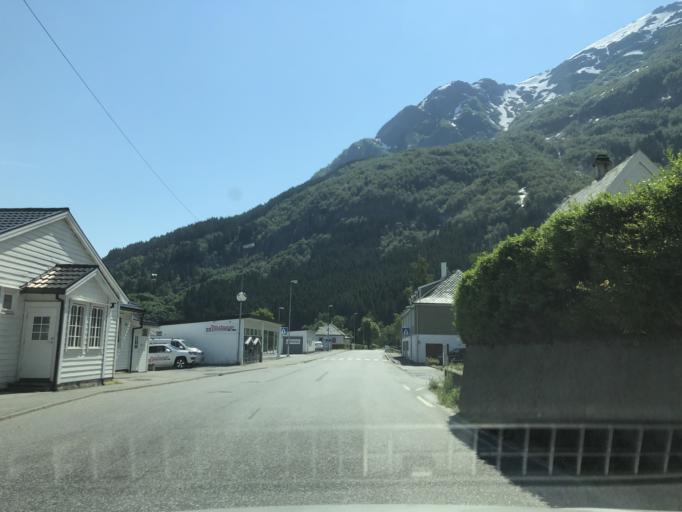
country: NO
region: Hordaland
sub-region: Odda
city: Odda
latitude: 60.0821
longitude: 6.5309
